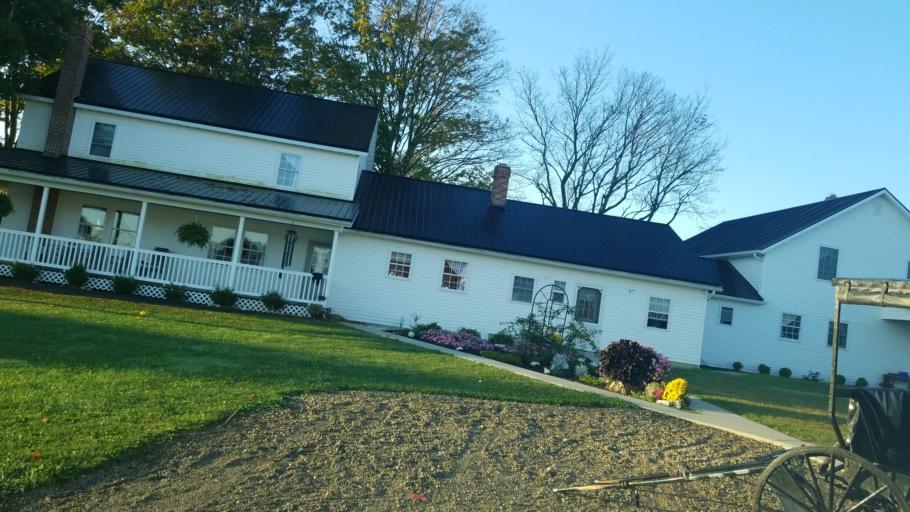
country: US
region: Ohio
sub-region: Knox County
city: Fredericktown
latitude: 40.5250
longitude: -82.6773
